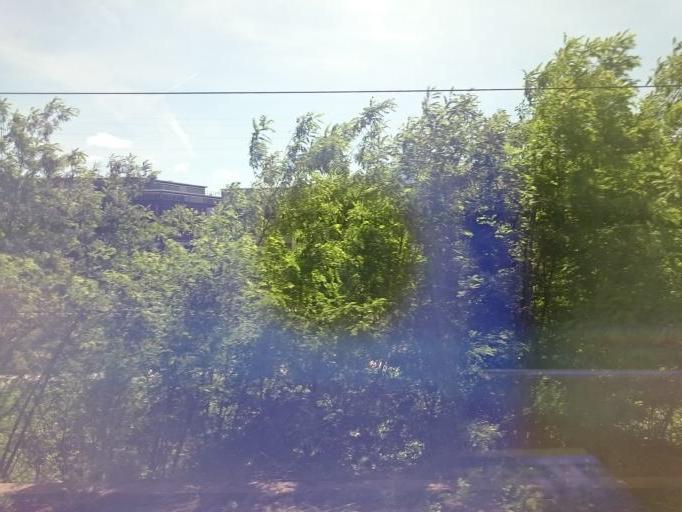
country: IT
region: Trentino-Alto Adige
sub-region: Bolzano
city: Varna
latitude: 46.7597
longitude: 11.6352
